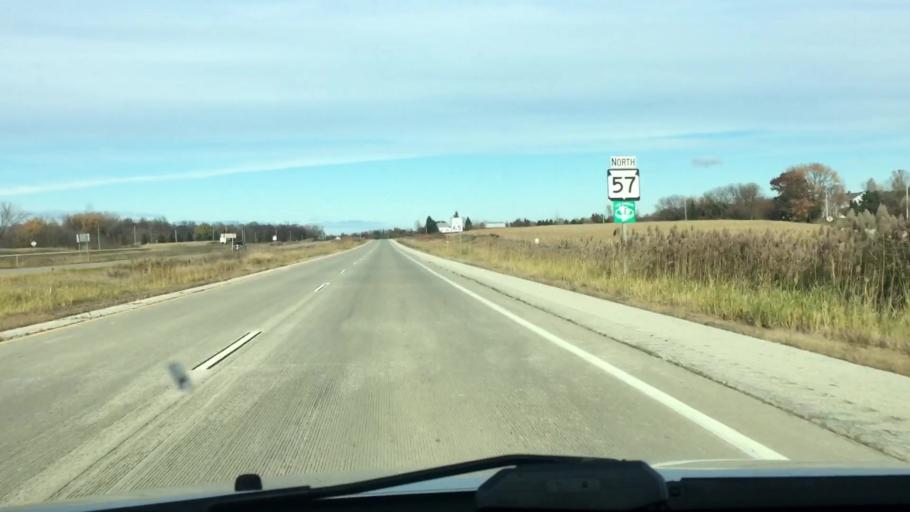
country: US
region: Wisconsin
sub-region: Kewaunee County
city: Luxemburg
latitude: 44.6596
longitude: -87.7463
